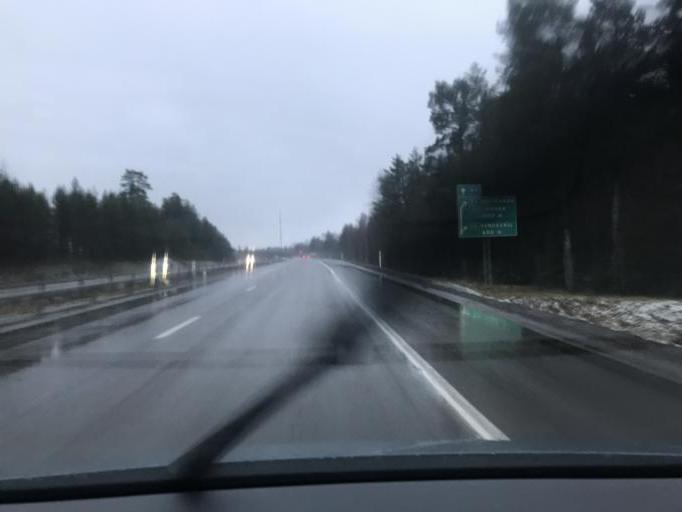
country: SE
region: Norrbotten
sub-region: Lulea Kommun
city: Gammelstad
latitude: 65.6306
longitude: 22.0419
